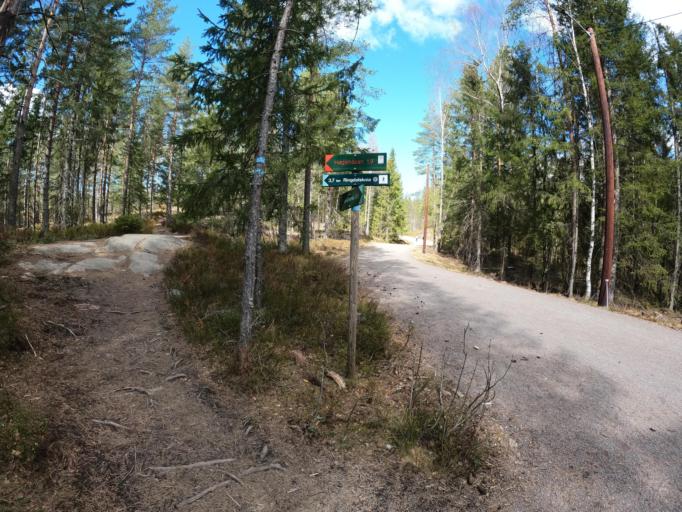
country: NO
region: Akershus
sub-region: Gjerdrum
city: Ask
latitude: 60.0161
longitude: 11.0022
